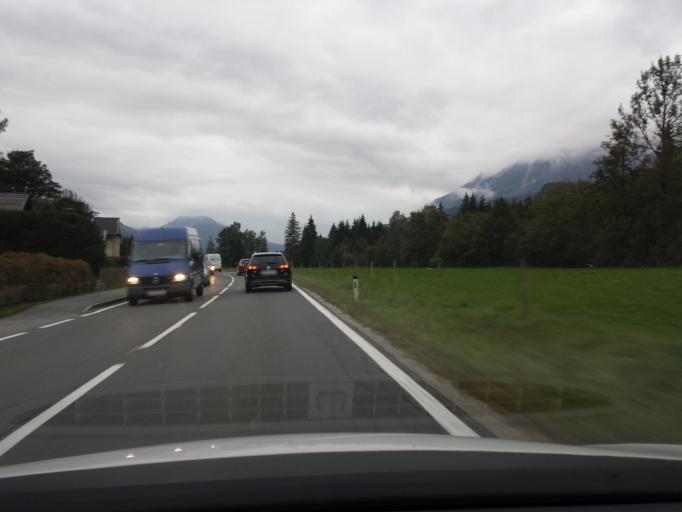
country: AT
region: Salzburg
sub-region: Politischer Bezirk Zell am See
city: Leogang
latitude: 47.4398
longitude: 12.8025
